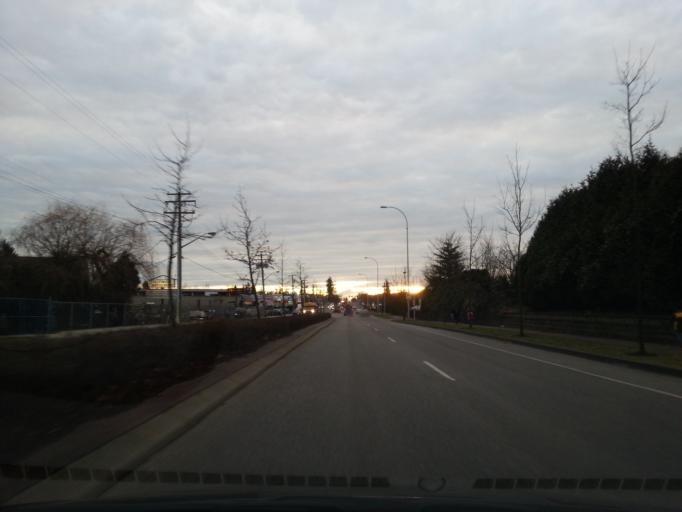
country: CA
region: British Columbia
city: Surrey
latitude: 49.1675
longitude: -122.8051
